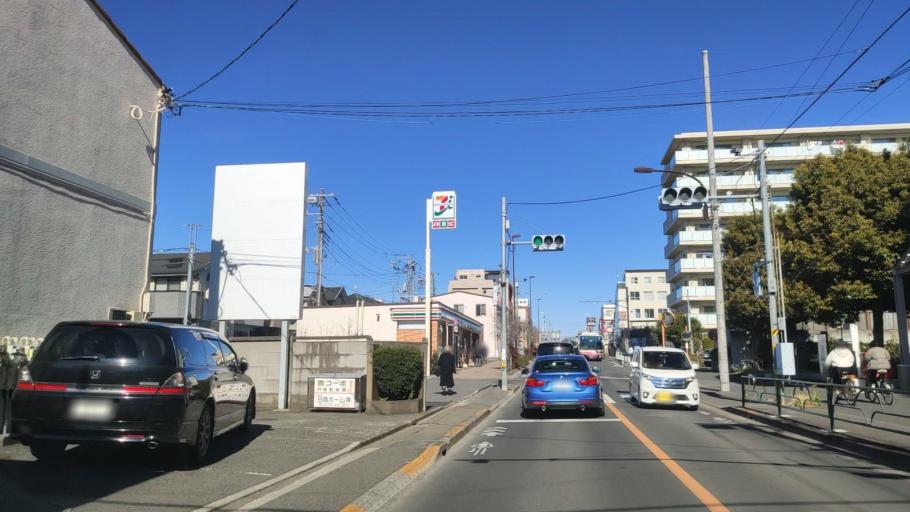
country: JP
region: Tokyo
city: Mitaka-shi
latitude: 35.6892
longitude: 139.5691
